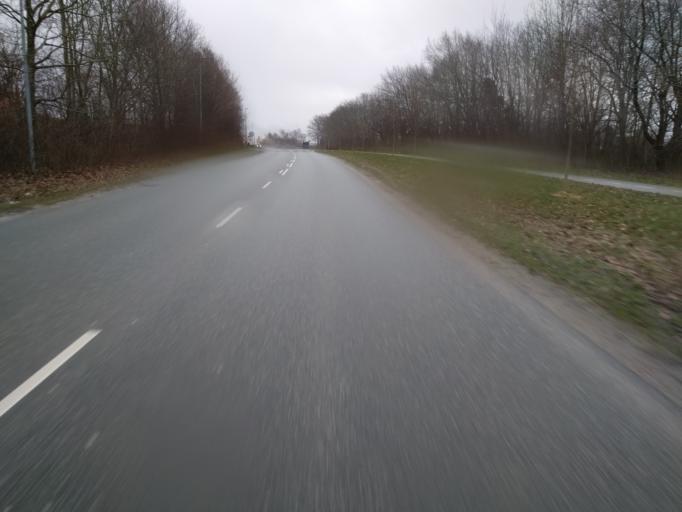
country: DK
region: Central Jutland
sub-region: Viborg Kommune
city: Viborg
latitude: 56.4551
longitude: 9.4455
